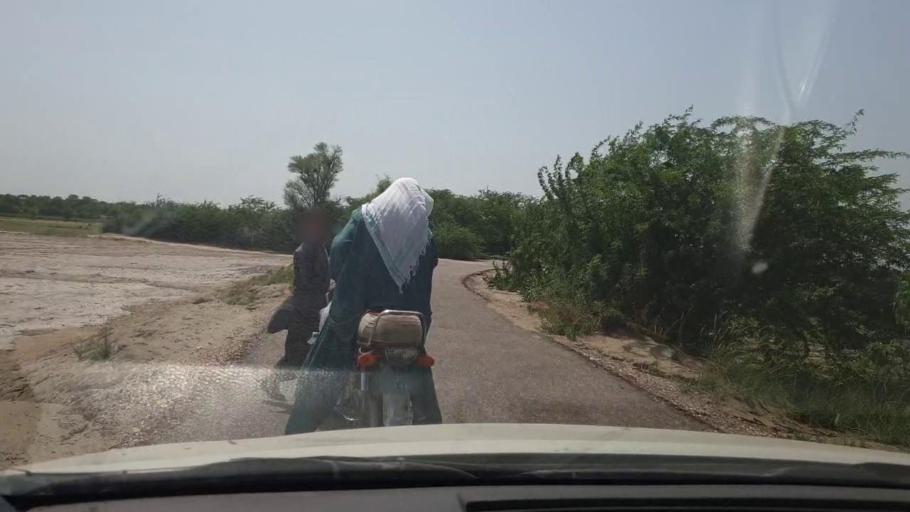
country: PK
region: Sindh
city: Rohri
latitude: 27.5184
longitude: 69.0768
